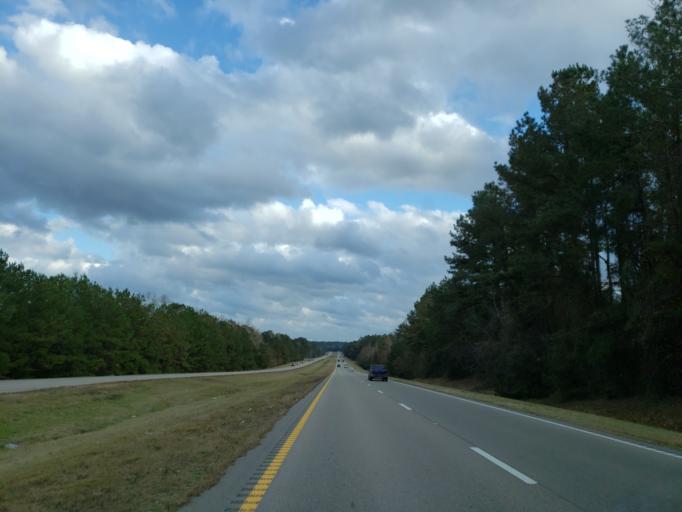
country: US
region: Mississippi
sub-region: Perry County
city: New Augusta
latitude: 31.2228
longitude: -89.1799
